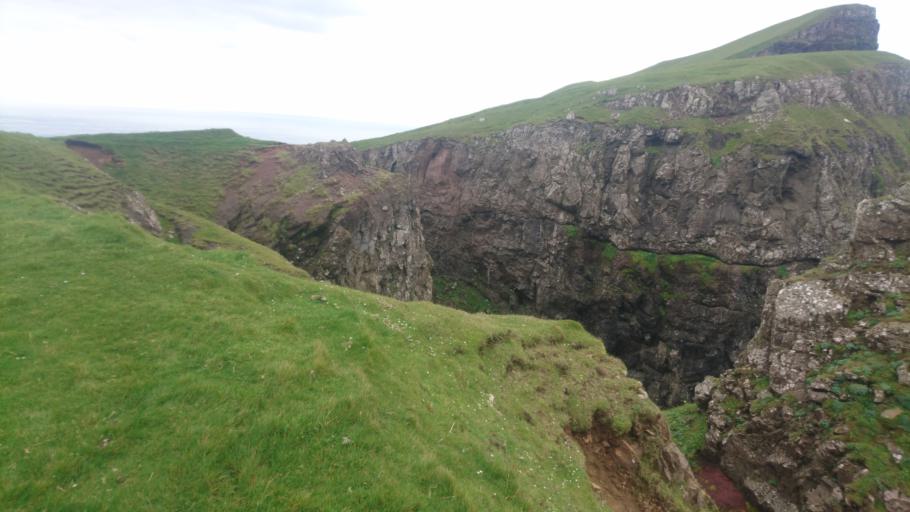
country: FO
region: Suduroy
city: Vagur
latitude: 61.4230
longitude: -6.7553
